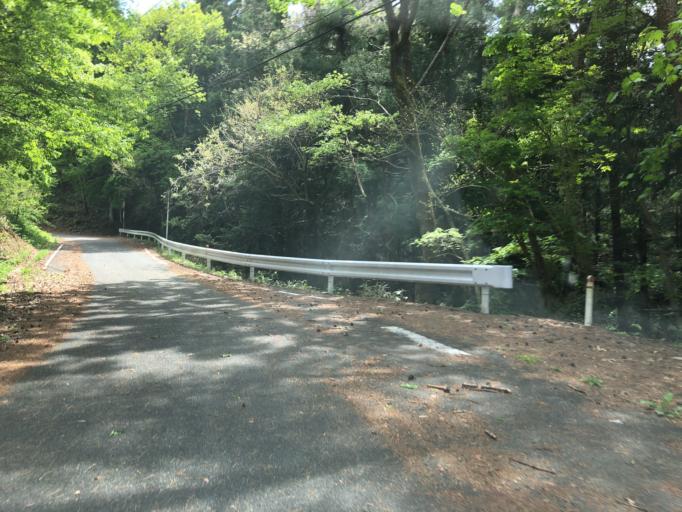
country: JP
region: Miyagi
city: Marumori
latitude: 37.7101
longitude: 140.7805
